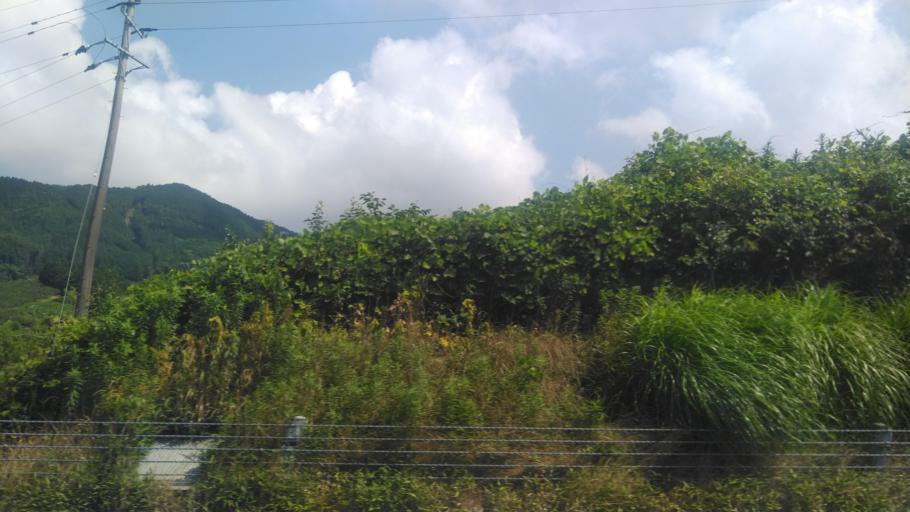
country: JP
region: Fukuoka
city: Tanushimarumachi-toyoki
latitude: 33.3696
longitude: 130.8029
